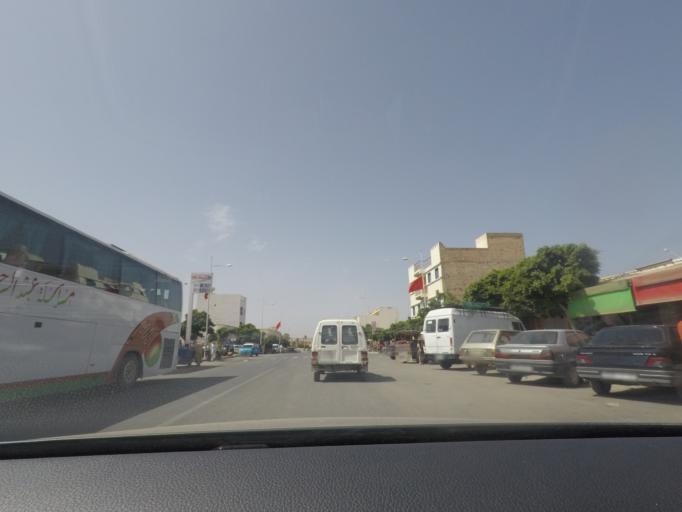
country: MA
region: Marrakech-Tensift-Al Haouz
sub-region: Essaouira
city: Tamanar
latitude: 31.0002
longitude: -9.6802
